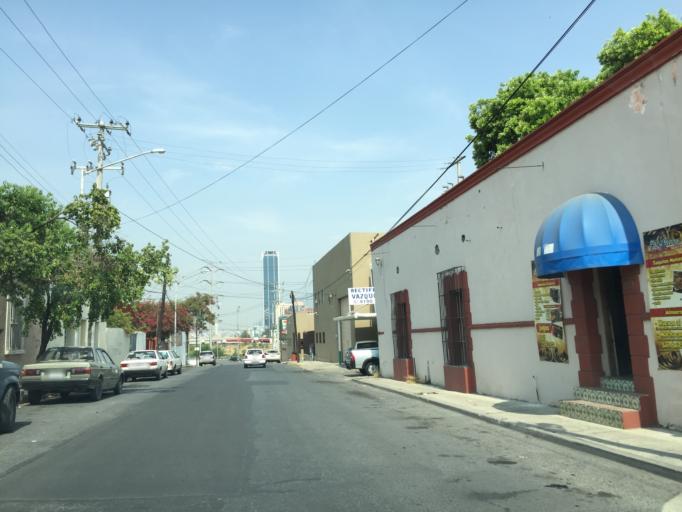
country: MX
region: Nuevo Leon
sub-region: Monterrey
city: Monterrey
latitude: 25.6621
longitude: -100.3039
